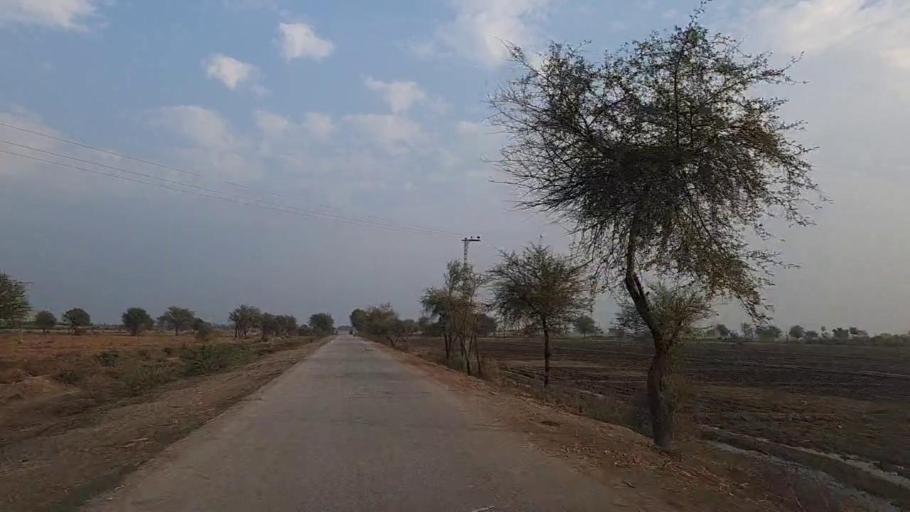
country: PK
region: Sindh
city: Mirwah Gorchani
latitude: 25.2985
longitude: 69.2229
